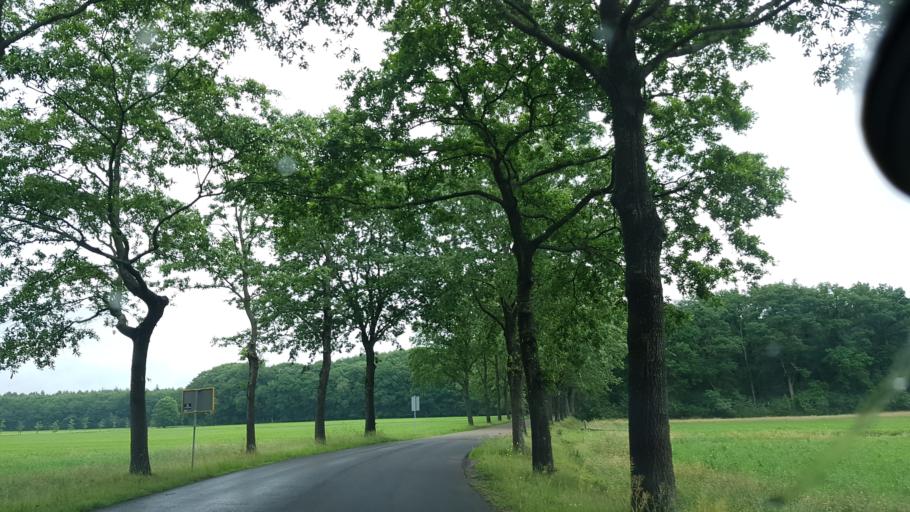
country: NL
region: Drenthe
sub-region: Gemeente Tynaarlo
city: Tynaarlo
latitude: 53.0485
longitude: 6.6095
